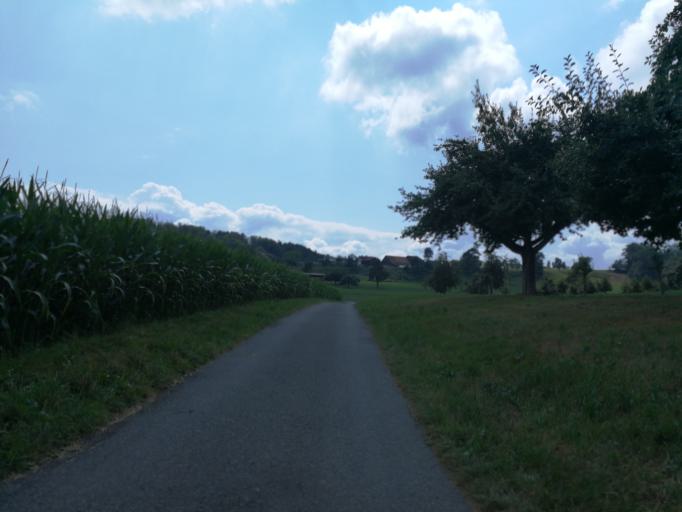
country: CH
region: Zurich
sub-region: Bezirk Hinwil
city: Binzikon
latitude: 47.2679
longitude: 8.7561
